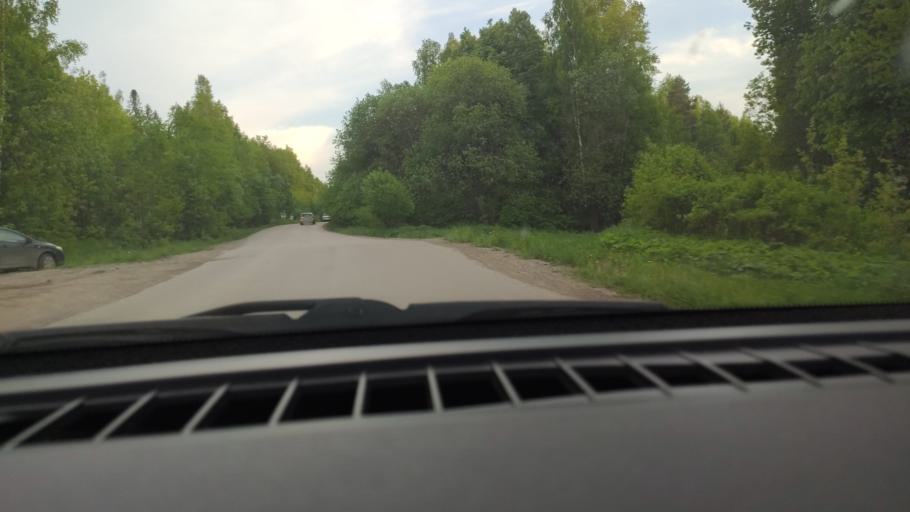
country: RU
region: Perm
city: Kondratovo
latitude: 58.0669
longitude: 56.0018
